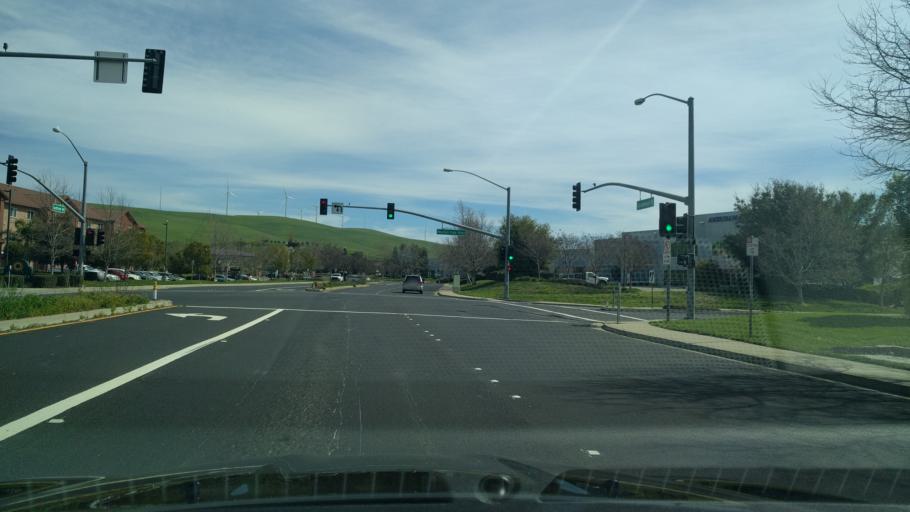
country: US
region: California
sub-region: Alameda County
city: Livermore
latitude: 37.7152
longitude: -121.7024
